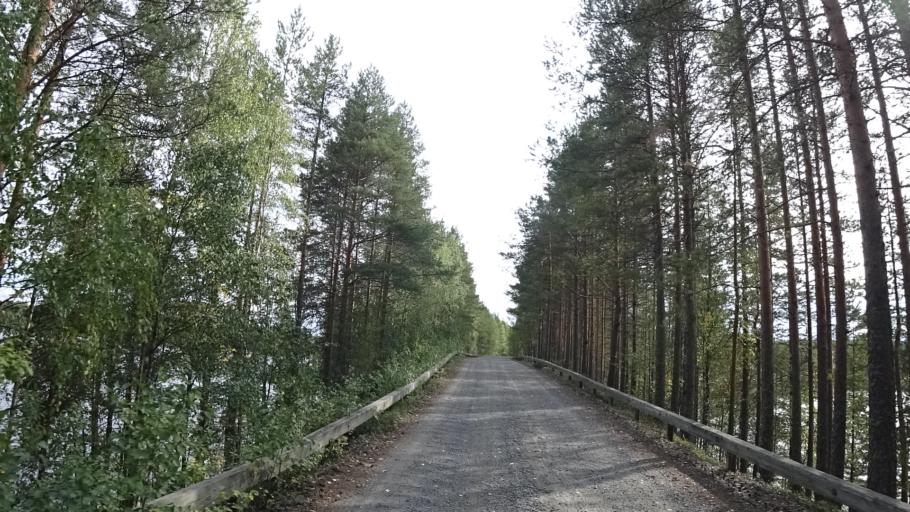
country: FI
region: North Karelia
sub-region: Joensuu
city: Ilomantsi
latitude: 62.6165
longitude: 31.1962
